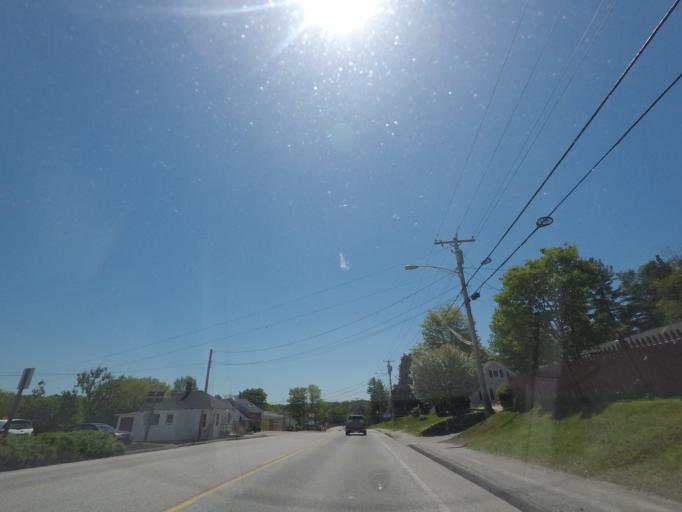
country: US
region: Maine
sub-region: Kennebec County
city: Farmingdale
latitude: 44.2602
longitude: -69.7783
